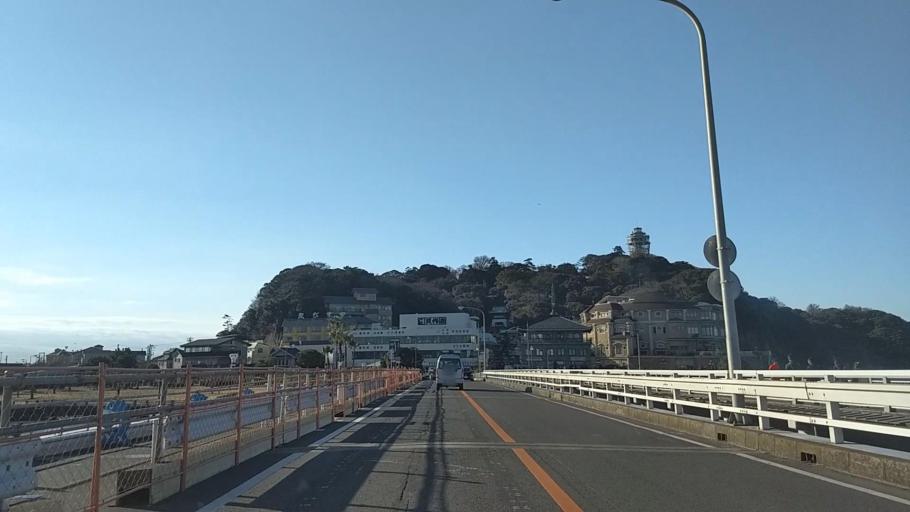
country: JP
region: Kanagawa
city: Fujisawa
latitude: 35.3037
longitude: 139.4820
